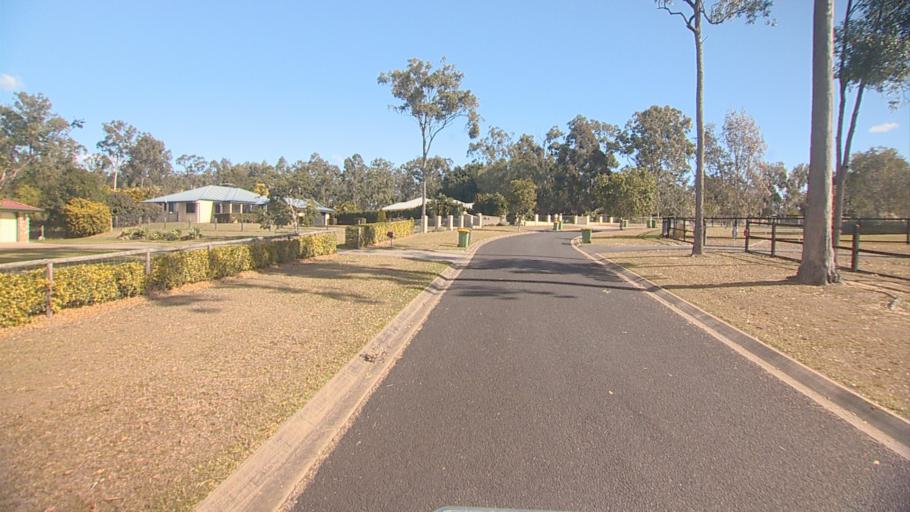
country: AU
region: Queensland
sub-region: Logan
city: North Maclean
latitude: -27.7494
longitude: 152.9376
